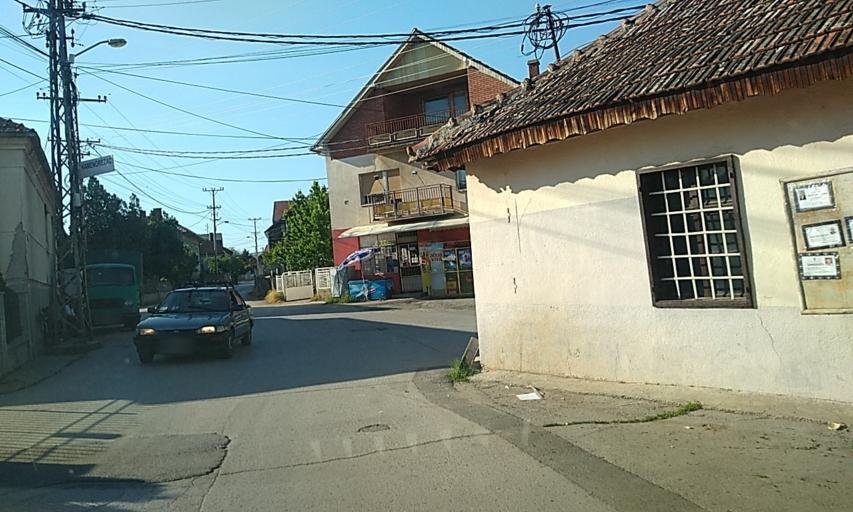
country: RS
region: Central Serbia
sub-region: Nisavski Okrug
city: Nis
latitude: 43.3280
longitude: 21.9500
